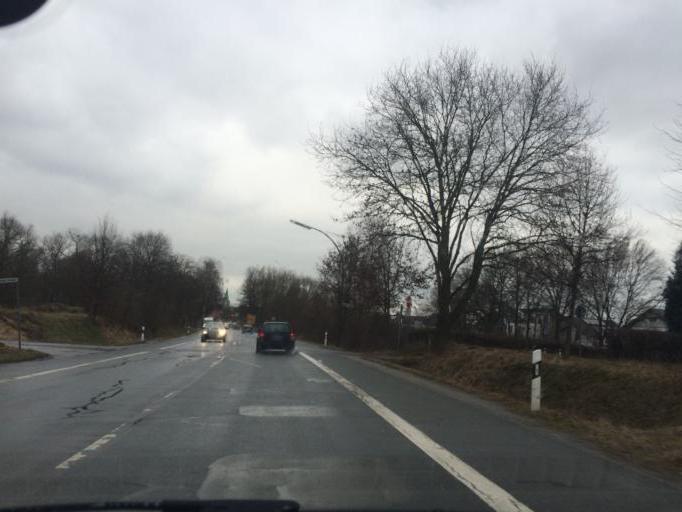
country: DE
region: North Rhine-Westphalia
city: Dorsten
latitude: 51.6521
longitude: 6.9666
